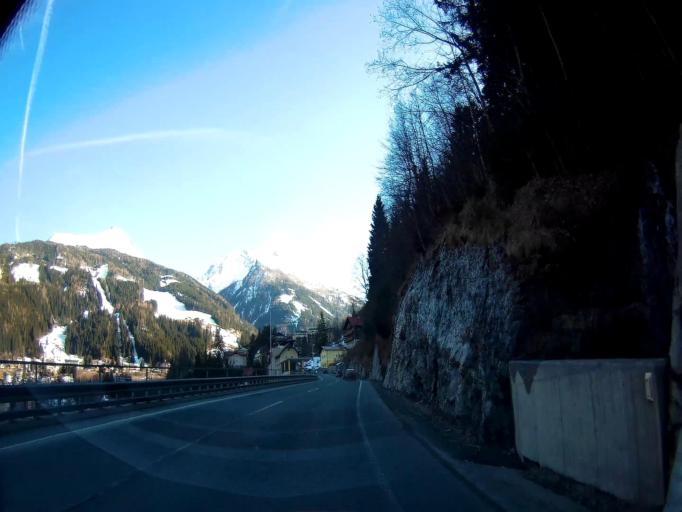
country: AT
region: Salzburg
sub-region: Politischer Bezirk Sankt Johann im Pongau
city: Bad Gastein
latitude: 47.1231
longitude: 13.1312
